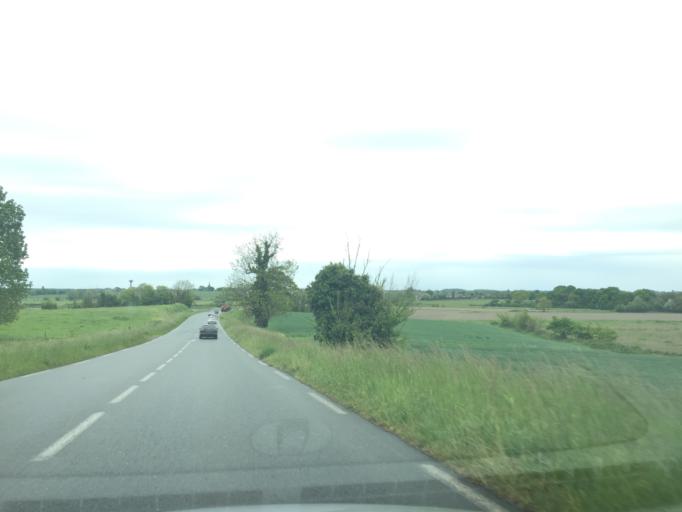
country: FR
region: Brittany
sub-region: Departement des Cotes-d'Armor
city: Ploubalay
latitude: 48.5766
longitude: -2.1705
